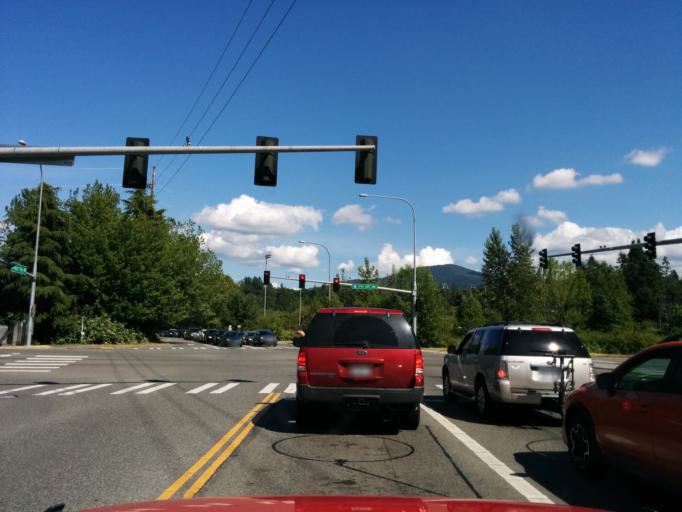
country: US
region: Washington
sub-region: King County
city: Issaquah
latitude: 47.5413
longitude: -122.0637
